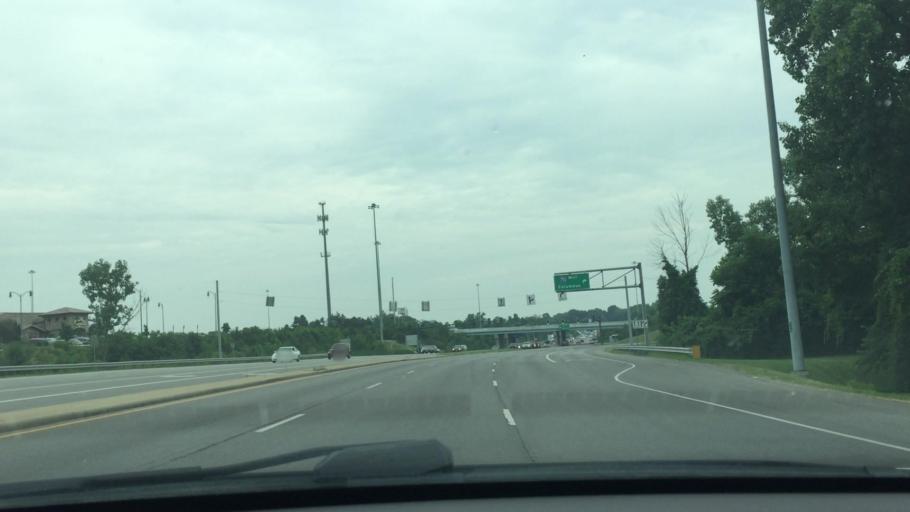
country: US
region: Ohio
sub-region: Franklin County
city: Reynoldsburg
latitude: 39.9362
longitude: -82.7900
